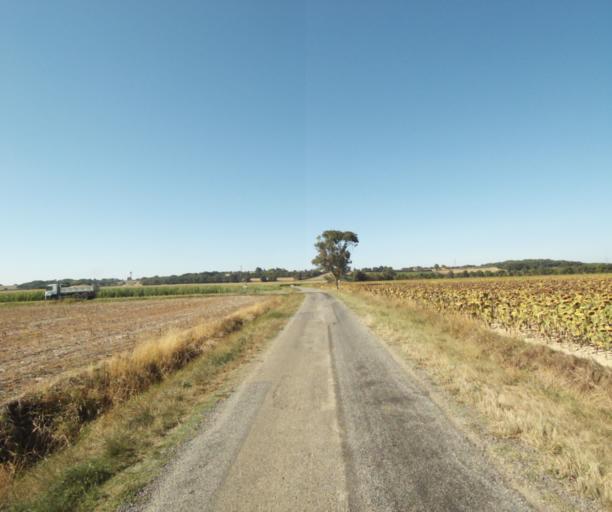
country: FR
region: Midi-Pyrenees
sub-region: Departement du Tarn-et-Garonne
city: Verdun-sur-Garonne
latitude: 43.8416
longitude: 1.2098
